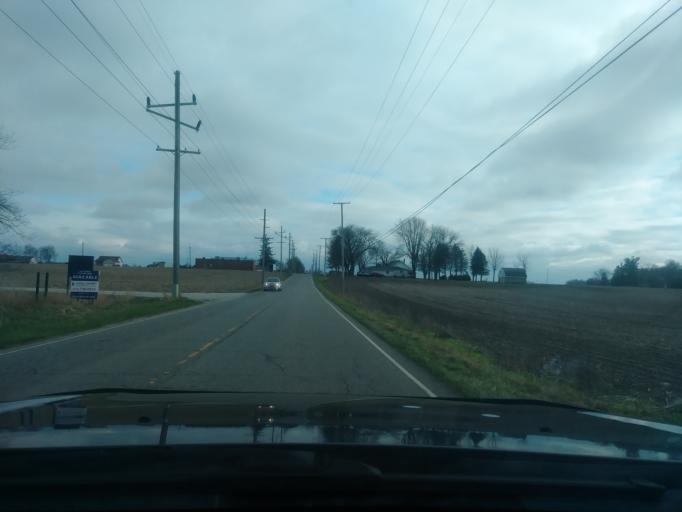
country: US
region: Indiana
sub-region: LaPorte County
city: LaPorte
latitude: 41.5946
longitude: -86.7979
